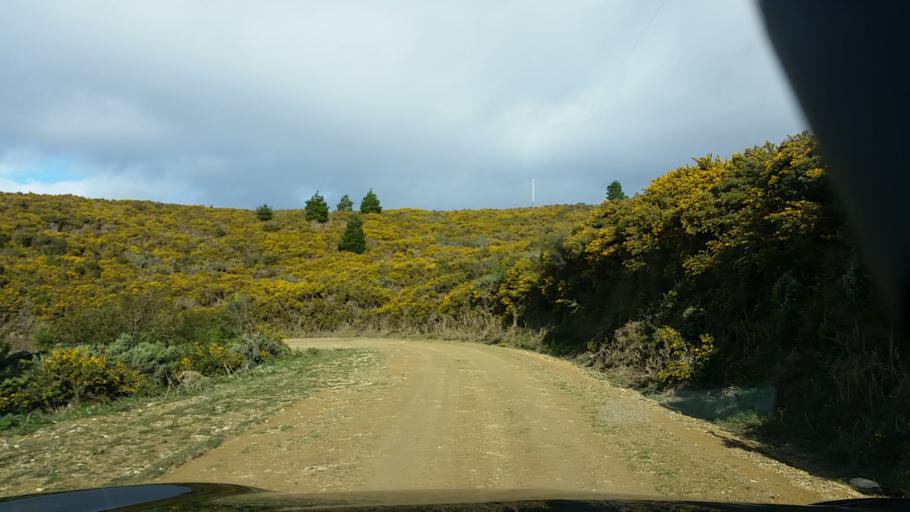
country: NZ
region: Marlborough
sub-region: Marlborough District
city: Picton
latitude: -40.9713
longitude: 173.8930
